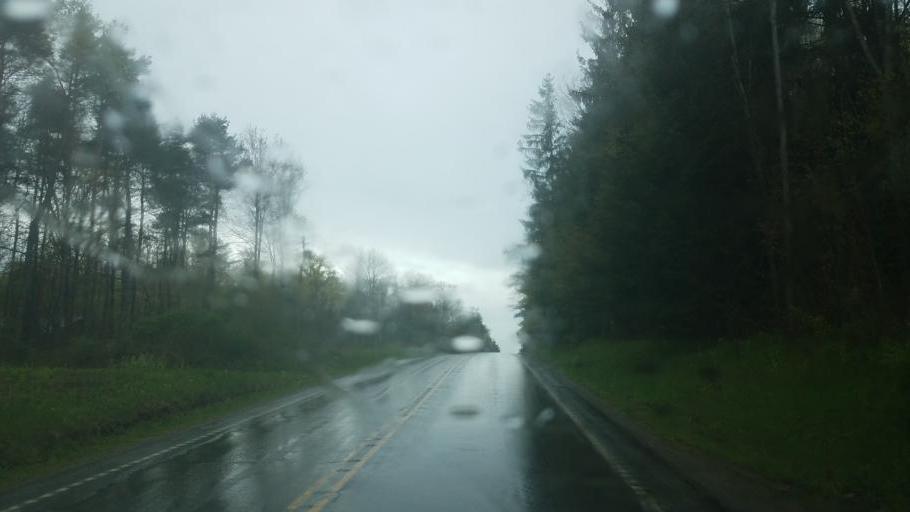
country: US
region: Pennsylvania
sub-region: Potter County
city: Galeton
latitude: 41.9122
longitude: -77.7558
